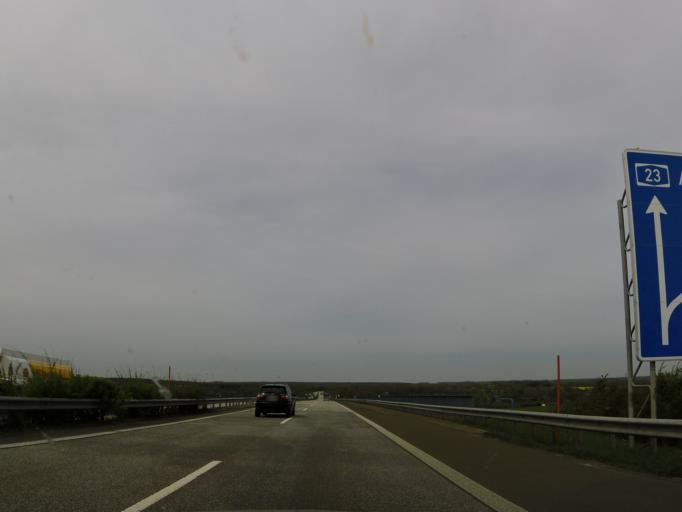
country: DE
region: Schleswig-Holstein
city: Schafstedt
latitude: 54.0715
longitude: 9.3065
